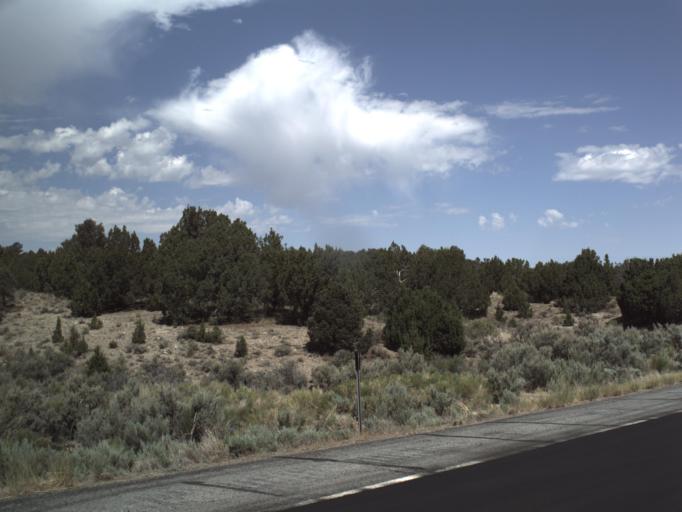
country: US
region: Utah
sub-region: Utah County
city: Eagle Mountain
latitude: 40.0059
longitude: -112.2758
